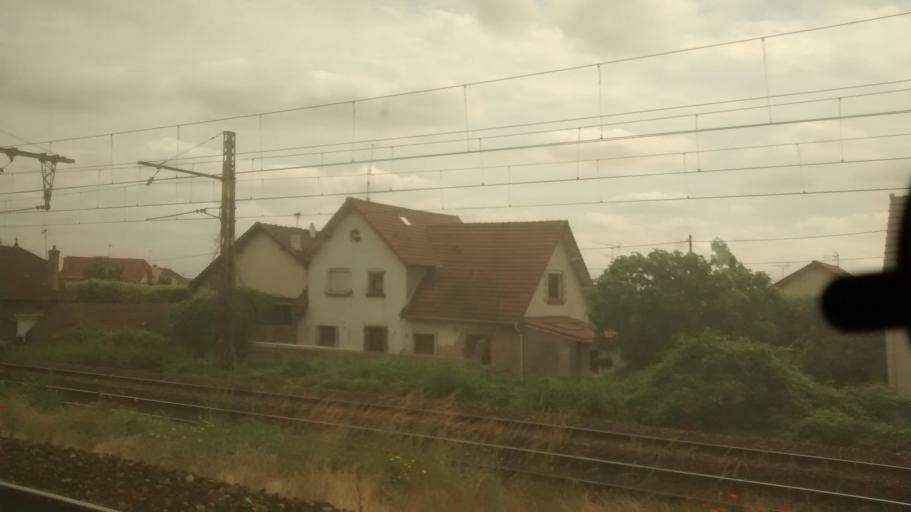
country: FR
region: Ile-de-France
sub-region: Departement du Val-de-Marne
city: Villeneuve-le-Roi
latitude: 48.7415
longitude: 2.4164
